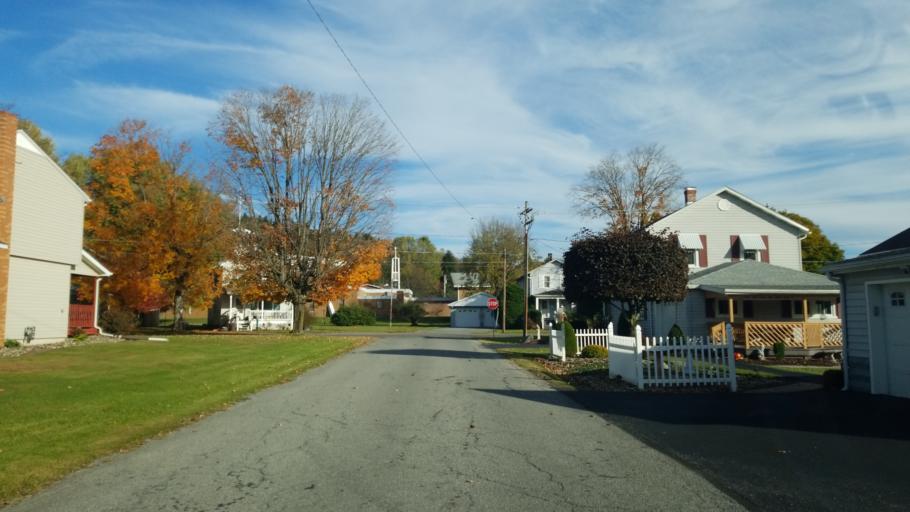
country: US
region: Pennsylvania
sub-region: Jefferson County
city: Brockway
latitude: 41.2479
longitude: -78.7845
